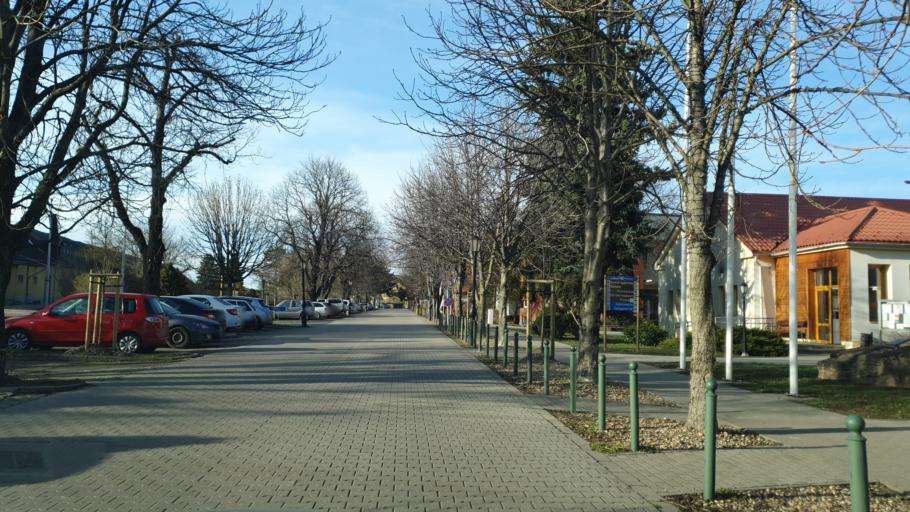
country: HU
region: Fejer
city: Etyek
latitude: 47.5013
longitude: 18.7522
